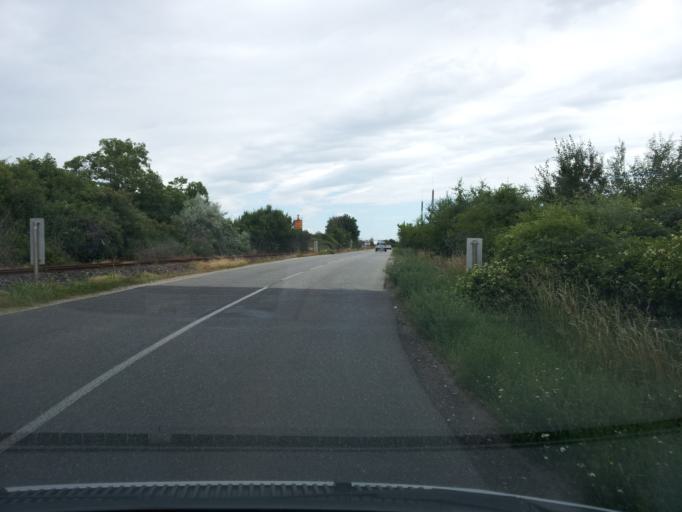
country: HU
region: Veszprem
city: Liter
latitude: 47.0885
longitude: 18.0358
